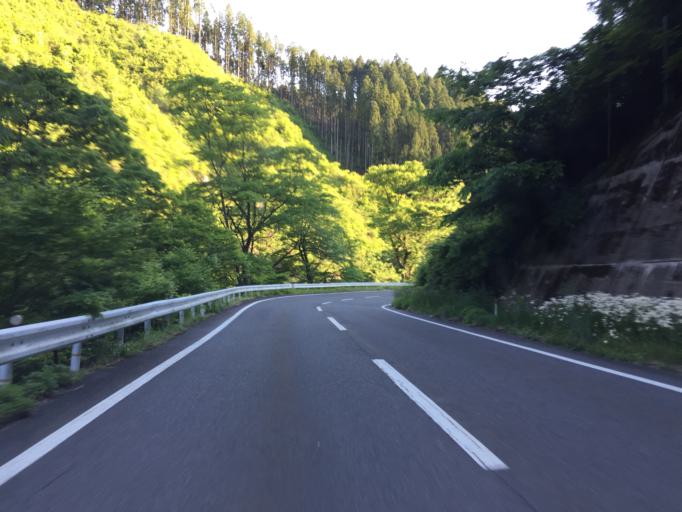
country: JP
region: Ibaraki
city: Daigo
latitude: 36.9279
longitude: 140.4805
